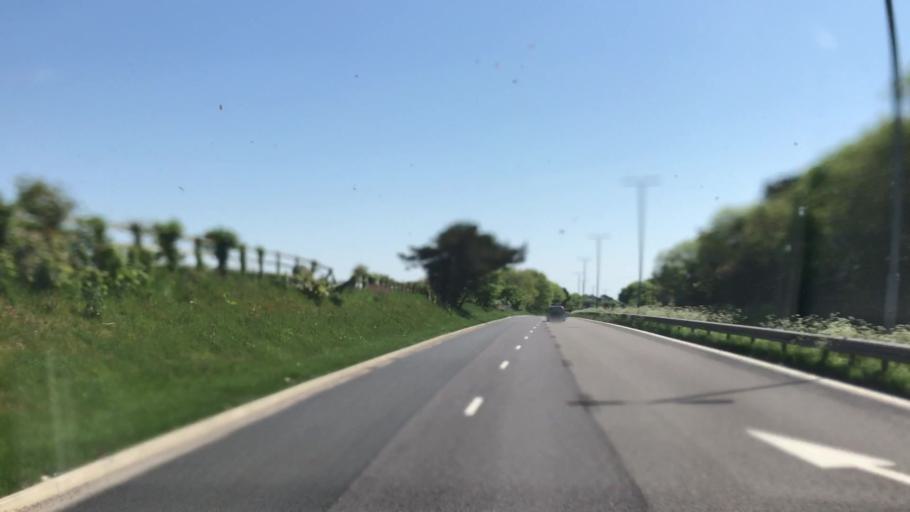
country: GB
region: England
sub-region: Cornwall
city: Chacewater
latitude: 50.2644
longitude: -5.1166
